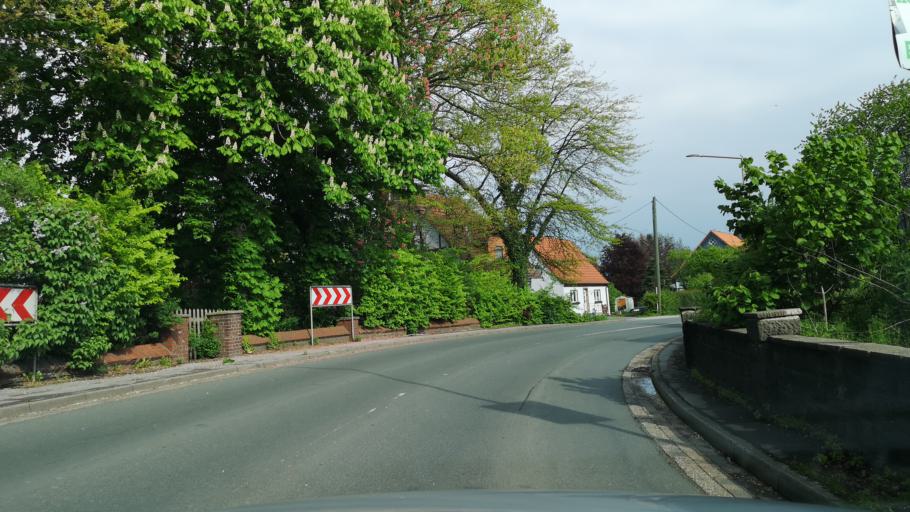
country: DE
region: North Rhine-Westphalia
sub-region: Regierungsbezirk Arnsberg
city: Holzwickede
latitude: 51.4447
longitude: 7.6298
